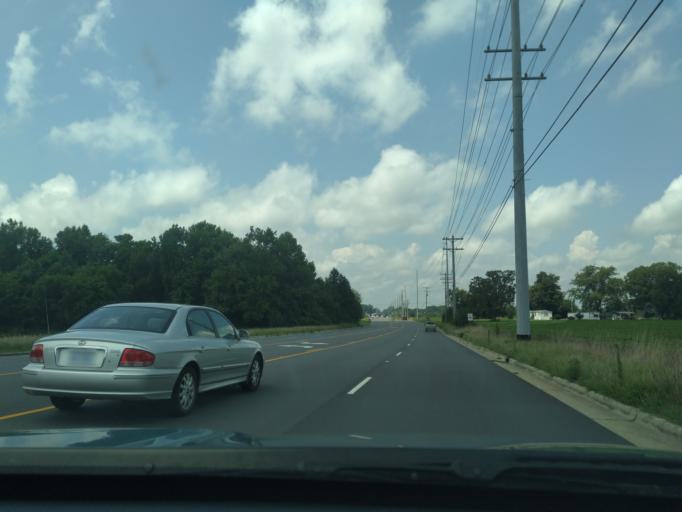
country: US
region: North Carolina
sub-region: Nash County
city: Rocky Mount
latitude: 35.9924
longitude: -77.8245
